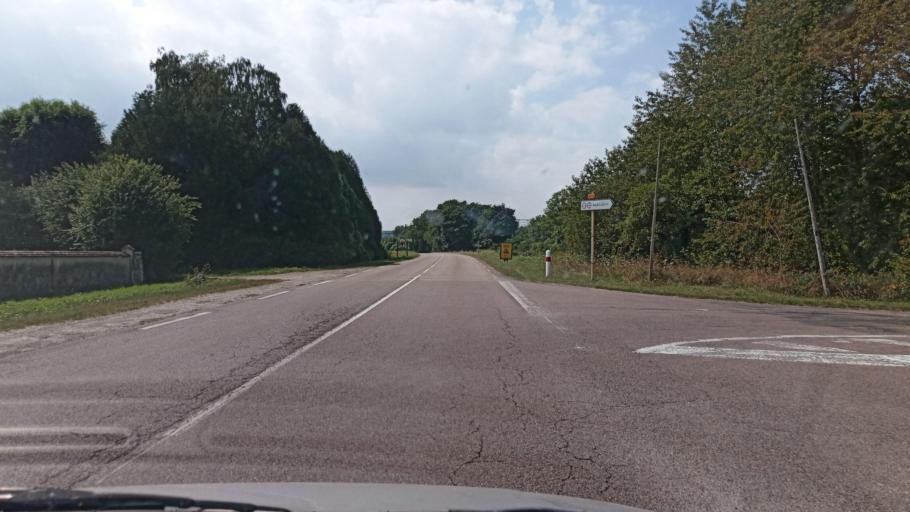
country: FR
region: Bourgogne
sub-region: Departement de l'Yonne
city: Veron
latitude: 48.1146
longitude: 3.2697
